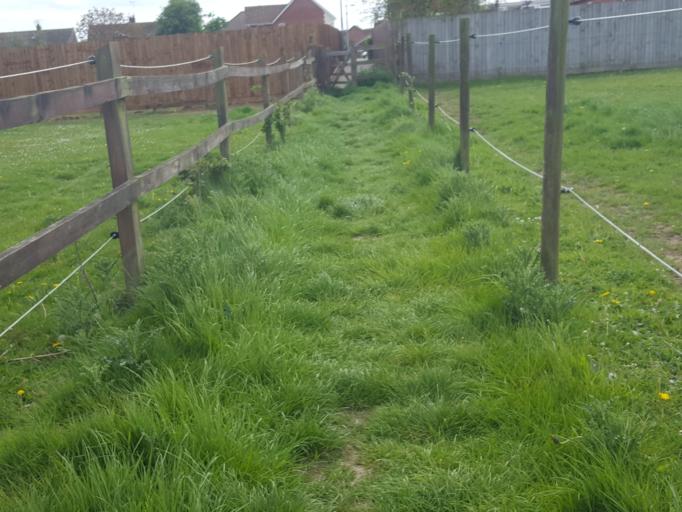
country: GB
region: England
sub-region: Essex
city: Frinton-on-Sea
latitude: 51.8438
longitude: 1.2156
